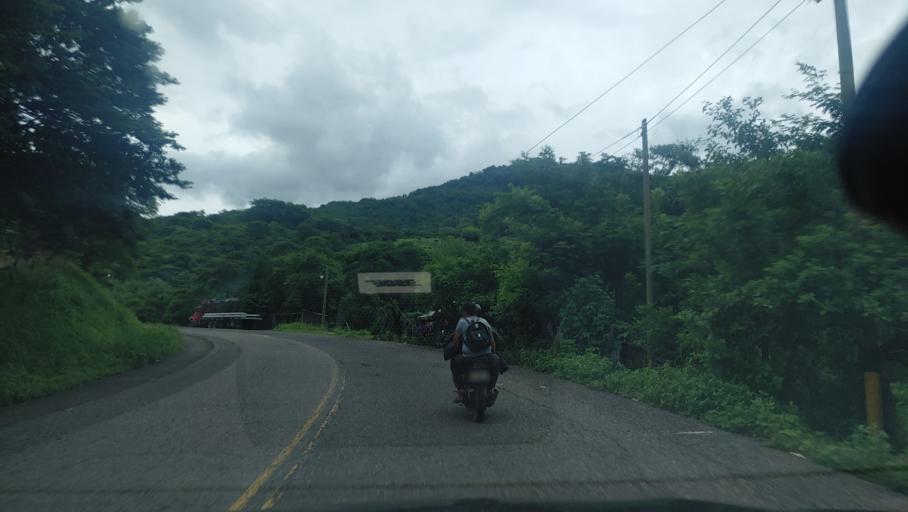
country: HN
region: Choluteca
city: Corpus
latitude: 13.3693
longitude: -87.0582
